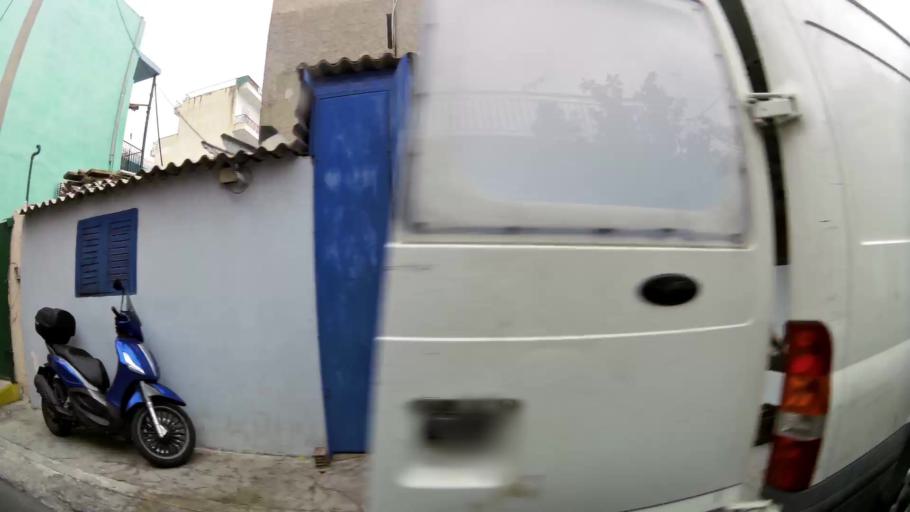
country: GR
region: Attica
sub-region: Nomos Piraios
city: Agios Ioannis Rentis
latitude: 37.9663
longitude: 23.6578
